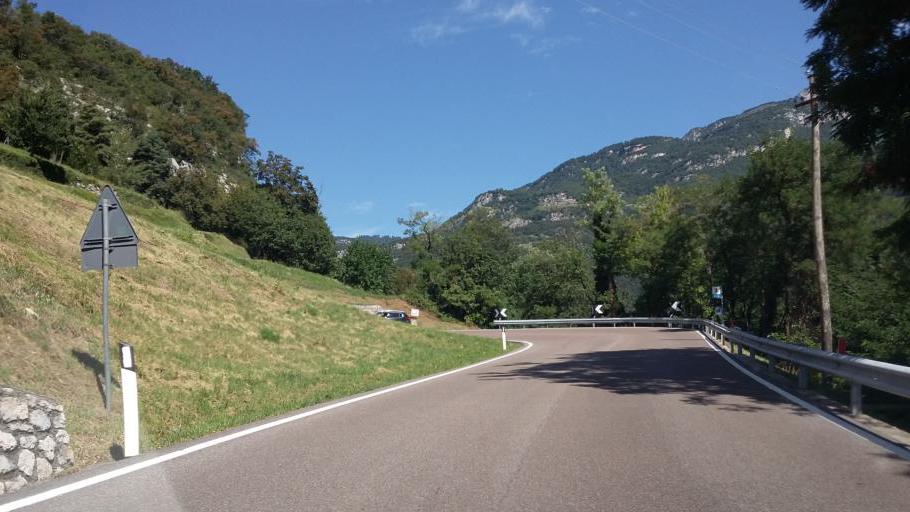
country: IT
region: Trentino-Alto Adige
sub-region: Provincia di Trento
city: Mori
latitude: 45.8446
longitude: 10.9728
